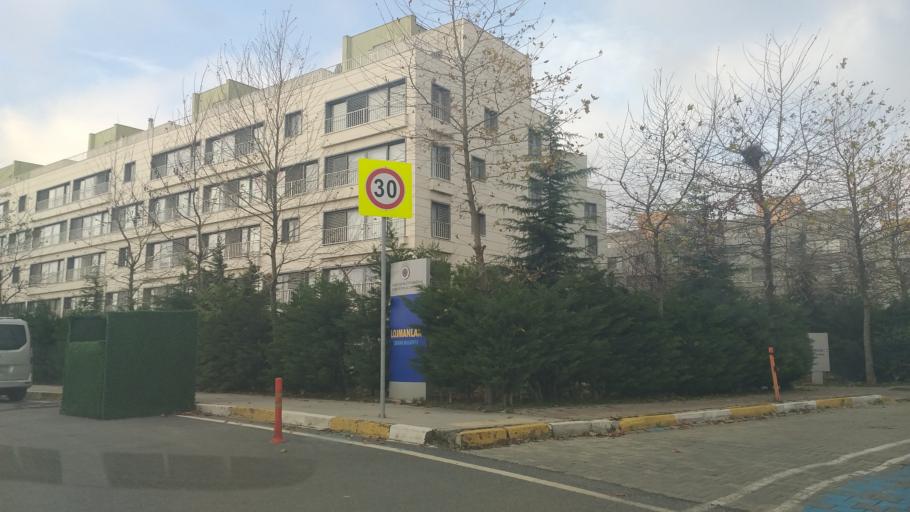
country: TR
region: Istanbul
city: merter keresteciler
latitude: 41.0296
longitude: 28.8893
